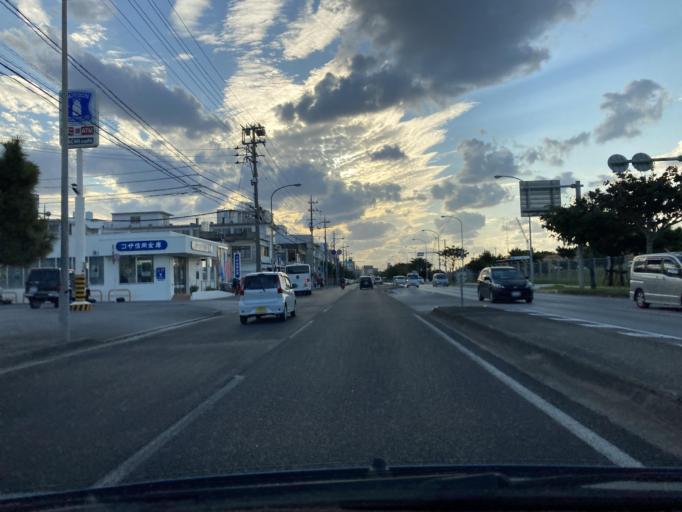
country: JP
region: Okinawa
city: Chatan
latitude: 26.2911
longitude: 127.7747
